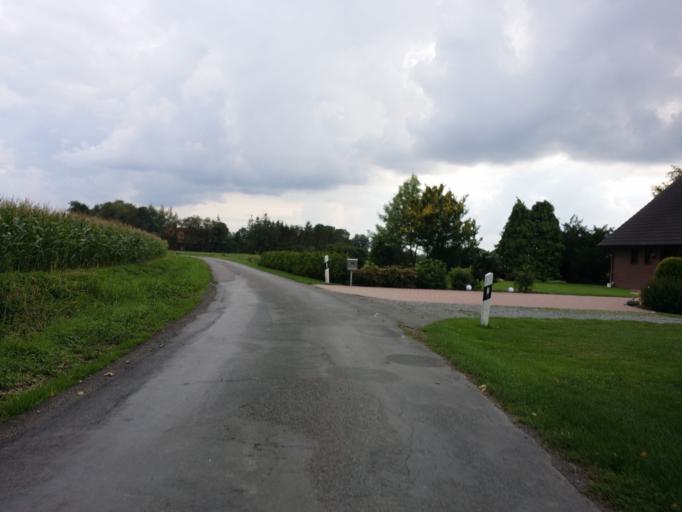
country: DE
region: Lower Saxony
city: Oederquart
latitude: 53.7718
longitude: 9.2139
